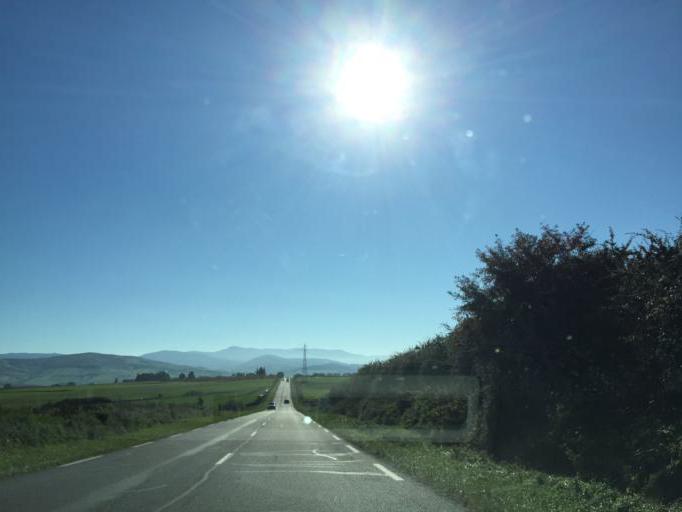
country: FR
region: Rhone-Alpes
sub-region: Departement du Rhone
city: Saint-Maurice-sur-Dargoire
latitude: 45.5666
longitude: 4.6438
